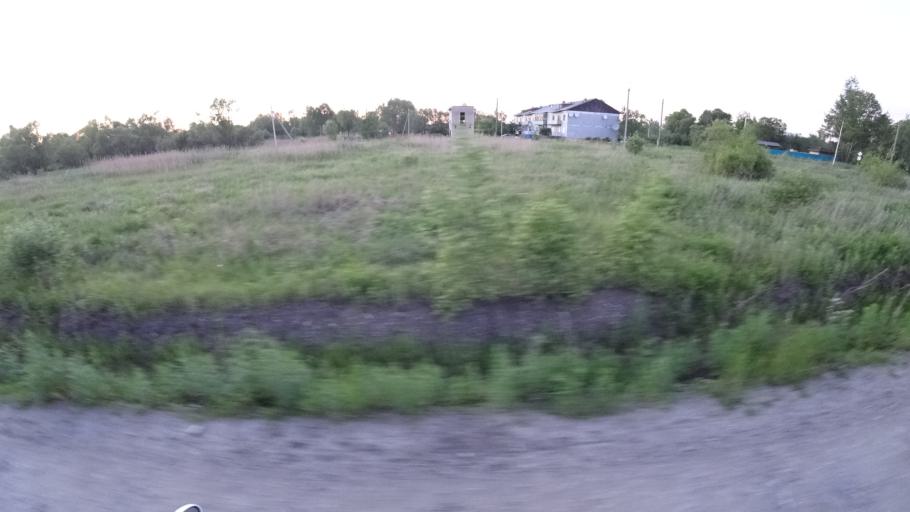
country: RU
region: Khabarovsk Krai
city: Khor
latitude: 47.8500
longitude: 134.9578
